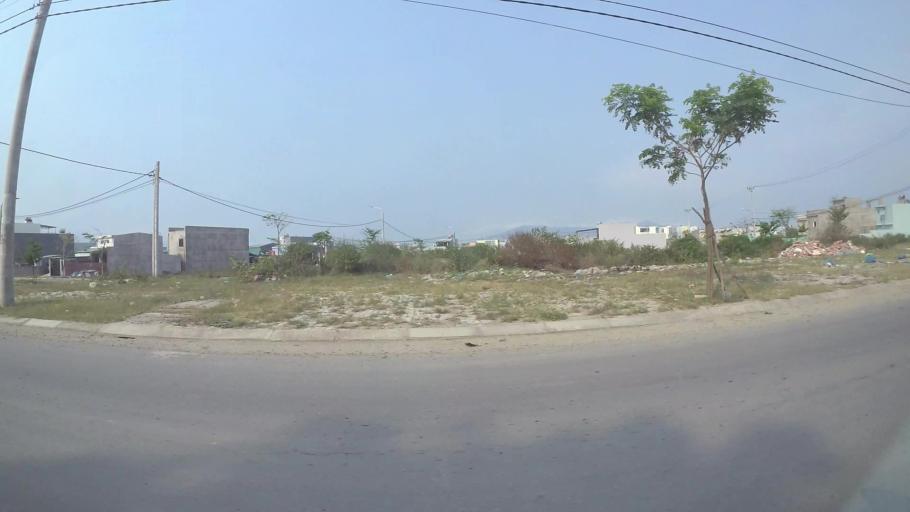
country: VN
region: Da Nang
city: Lien Chieu
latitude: 16.0410
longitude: 108.1678
